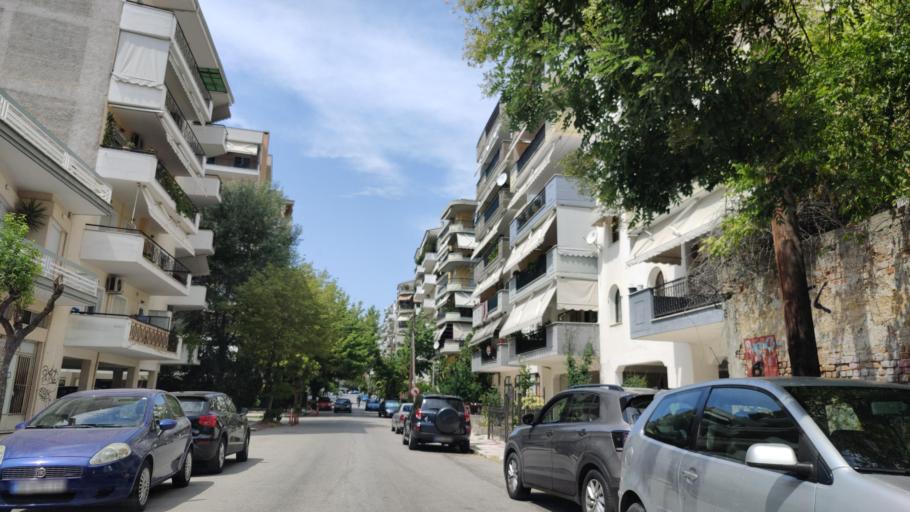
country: GR
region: Central Macedonia
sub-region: Nomos Serron
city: Serres
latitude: 41.0847
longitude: 23.5439
